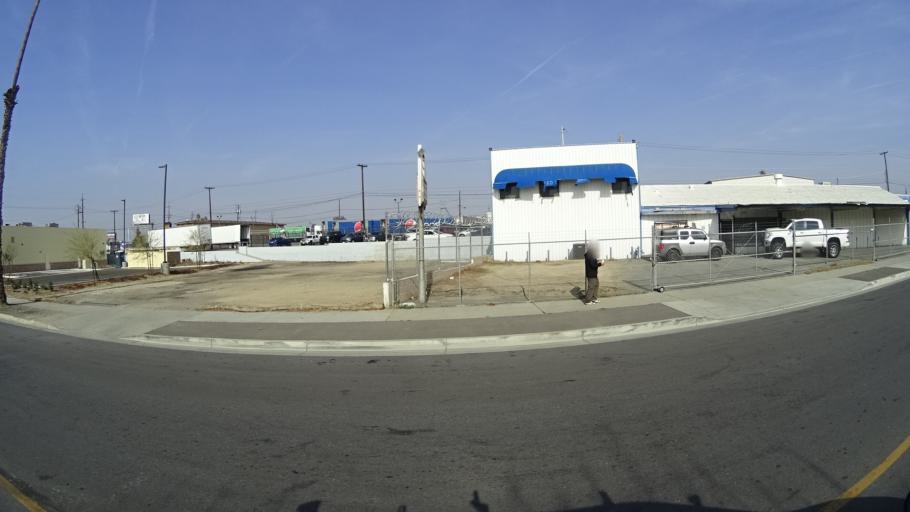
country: US
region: California
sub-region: Kern County
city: Bakersfield
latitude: 35.3763
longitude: -119.0015
